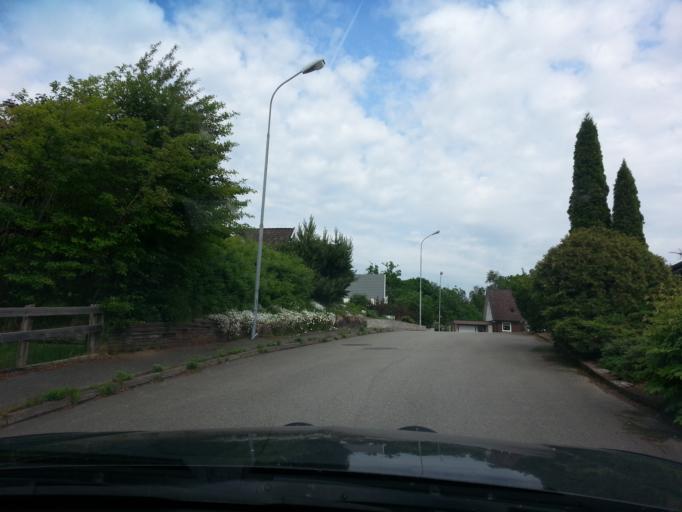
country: SE
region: Joenkoeping
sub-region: Vetlanda Kommun
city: Vetlanda
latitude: 57.2968
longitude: 15.1295
